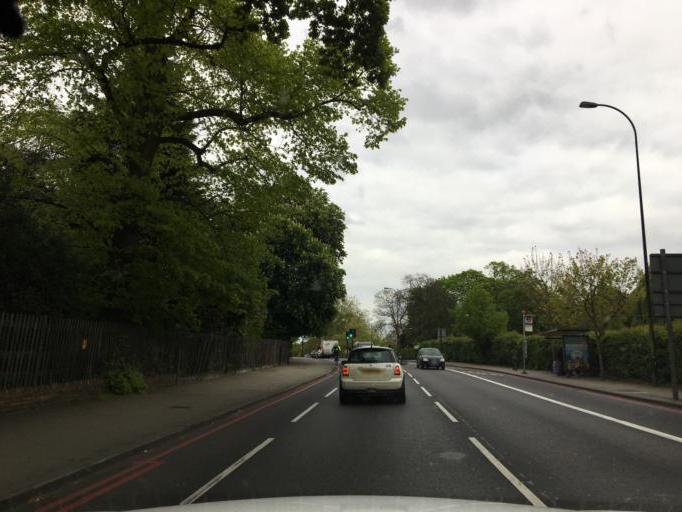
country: GB
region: England
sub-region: Greater London
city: Catford
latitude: 51.4408
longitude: -0.0631
